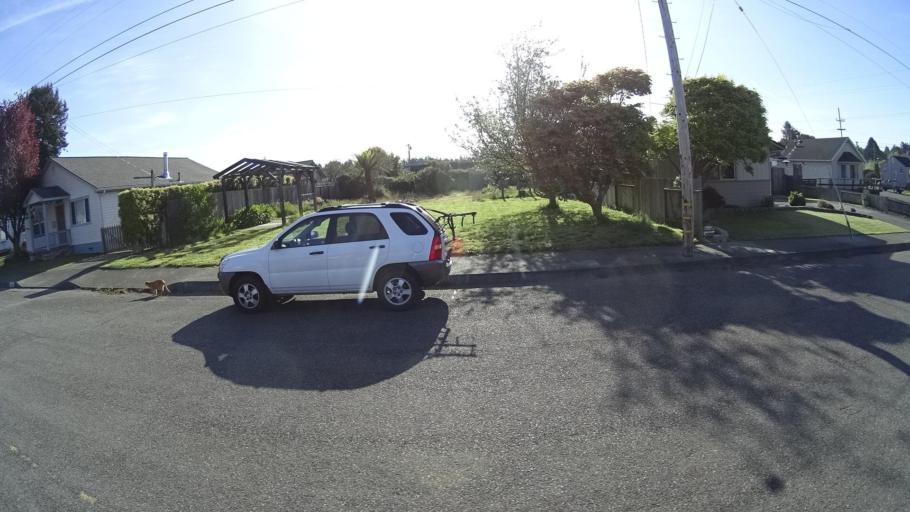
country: US
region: California
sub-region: Humboldt County
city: Bayview
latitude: 40.7717
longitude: -124.1659
